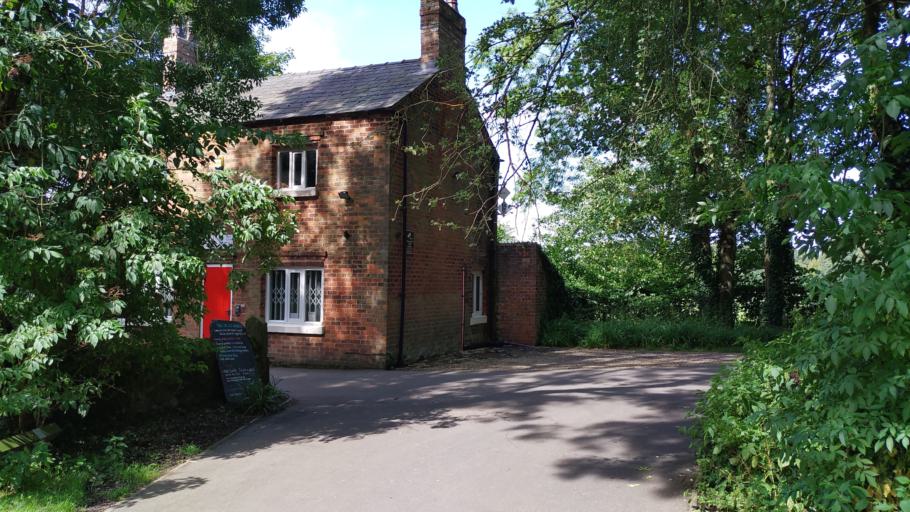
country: GB
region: England
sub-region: Lancashire
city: Leyland
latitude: 53.6828
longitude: -2.7022
